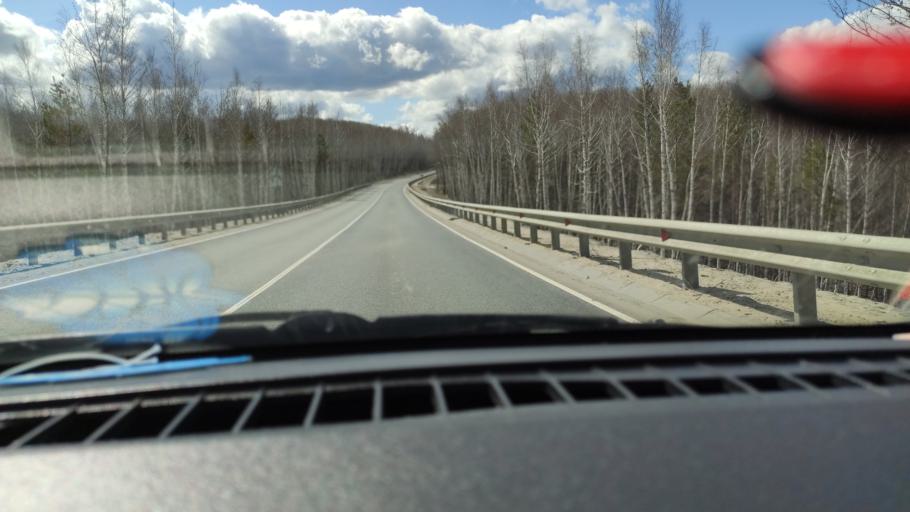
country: RU
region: Saratov
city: Khvalynsk
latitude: 52.4550
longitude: 48.0142
